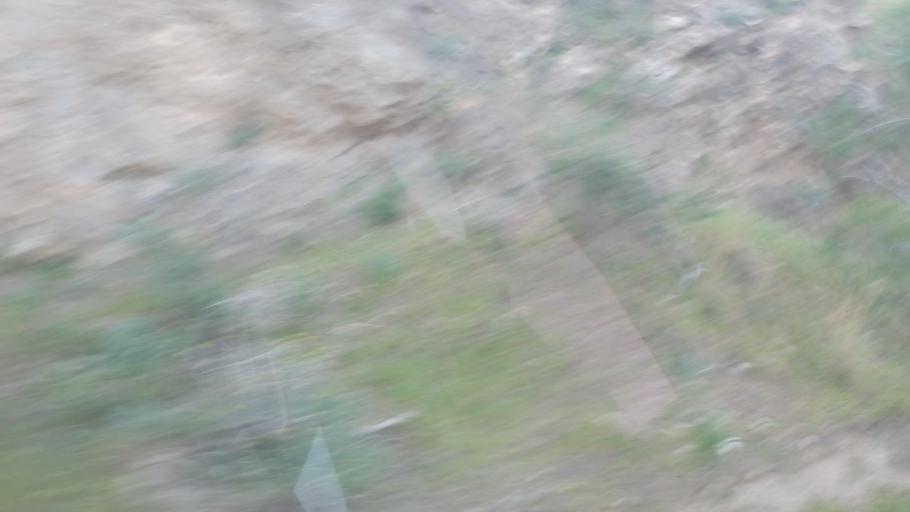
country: CY
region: Pafos
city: Polis
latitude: 34.9926
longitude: 32.3314
